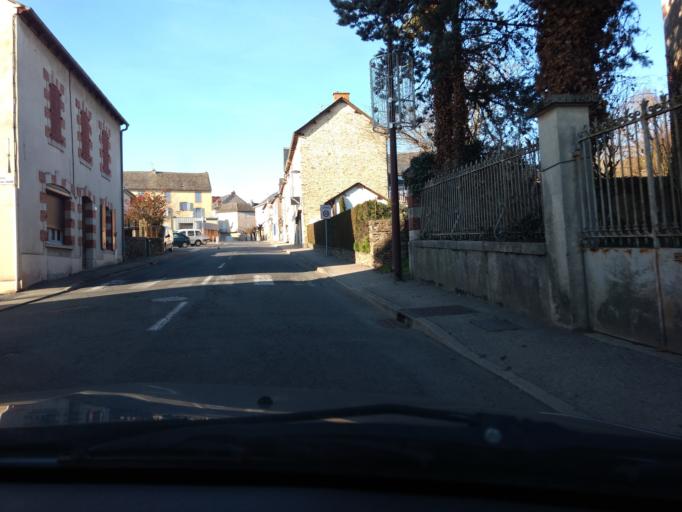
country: FR
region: Midi-Pyrenees
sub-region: Departement de l'Aveyron
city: Naucelle
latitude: 44.1973
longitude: 2.3434
